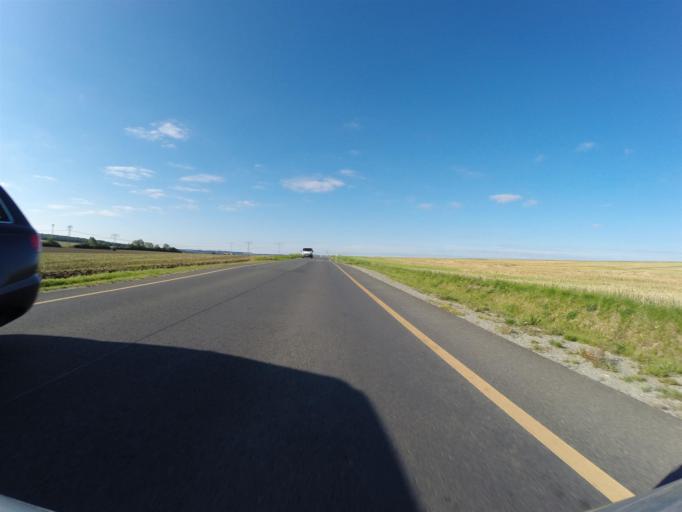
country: DE
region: Thuringia
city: Kleinschwabhausen
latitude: 50.9273
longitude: 11.4590
